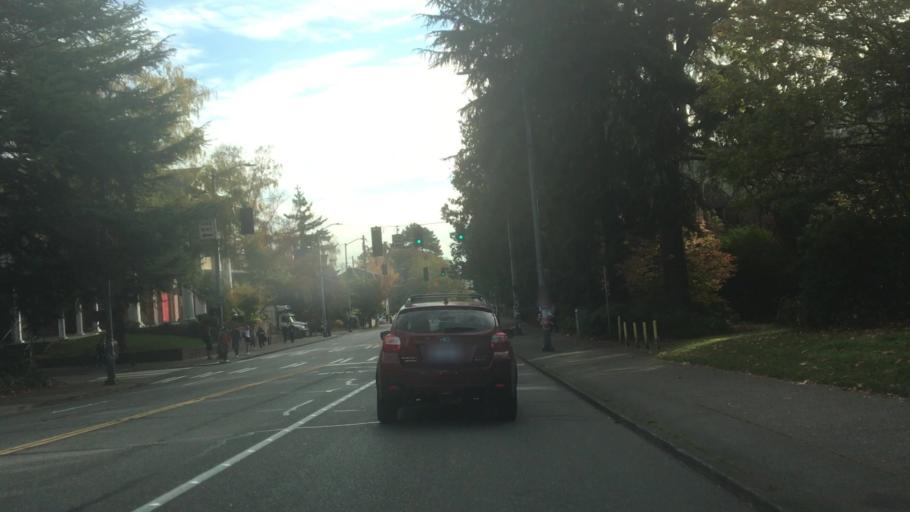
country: US
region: Washington
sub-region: King County
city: Seattle
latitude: 47.6612
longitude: -122.3078
